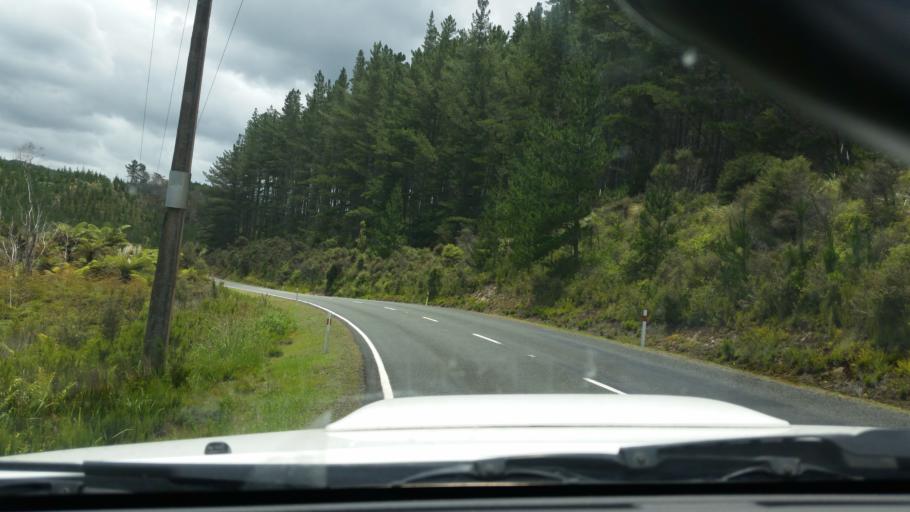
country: NZ
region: Northland
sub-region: Kaipara District
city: Dargaville
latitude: -35.8208
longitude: 173.7104
